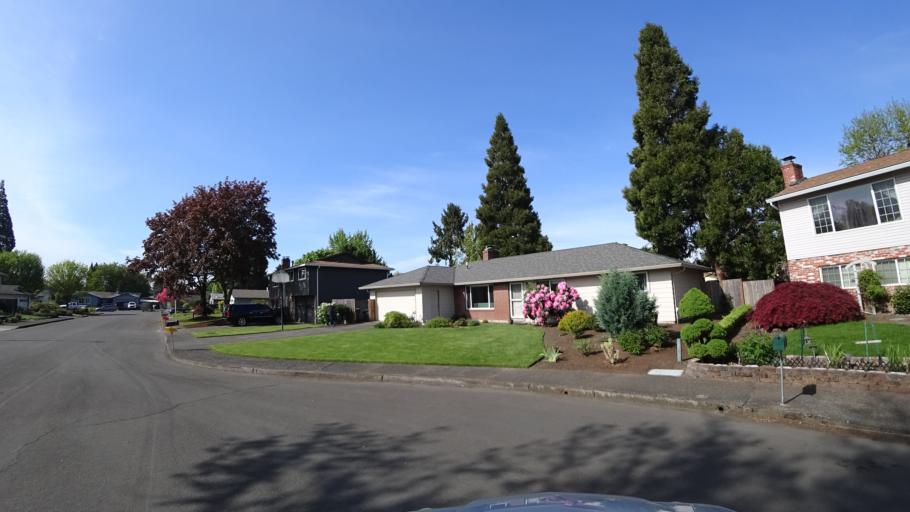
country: US
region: Oregon
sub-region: Washington County
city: Hillsboro
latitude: 45.5218
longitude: -122.9465
